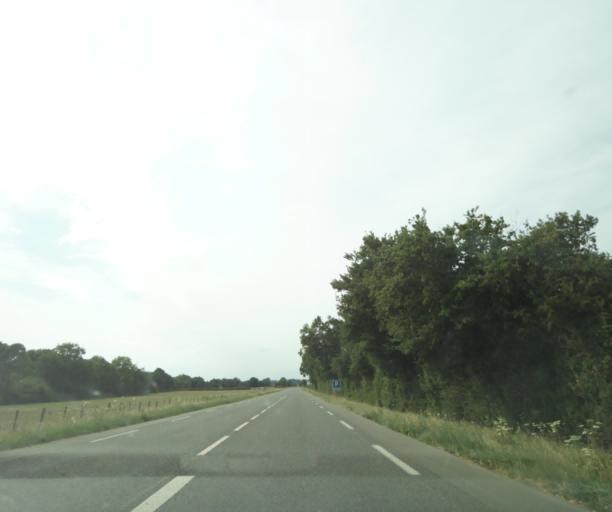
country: FR
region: Pays de la Loire
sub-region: Departement de la Sarthe
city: Chateau-du-Loir
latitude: 47.6699
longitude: 0.4628
